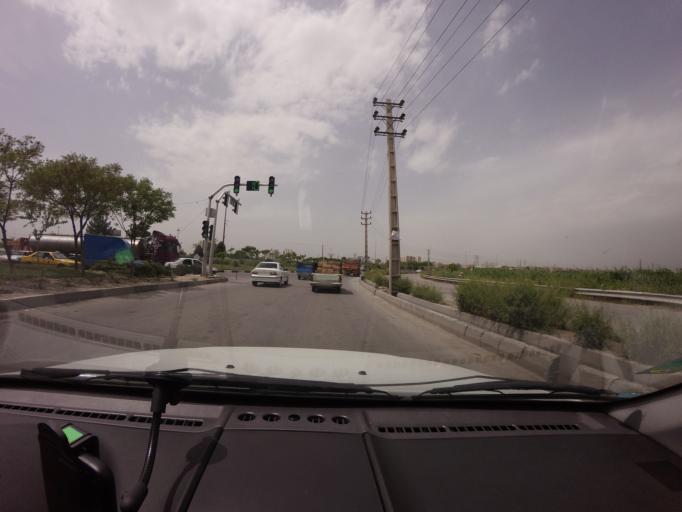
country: IR
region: Tehran
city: Eslamshahr
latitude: 35.5165
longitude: 51.2326
